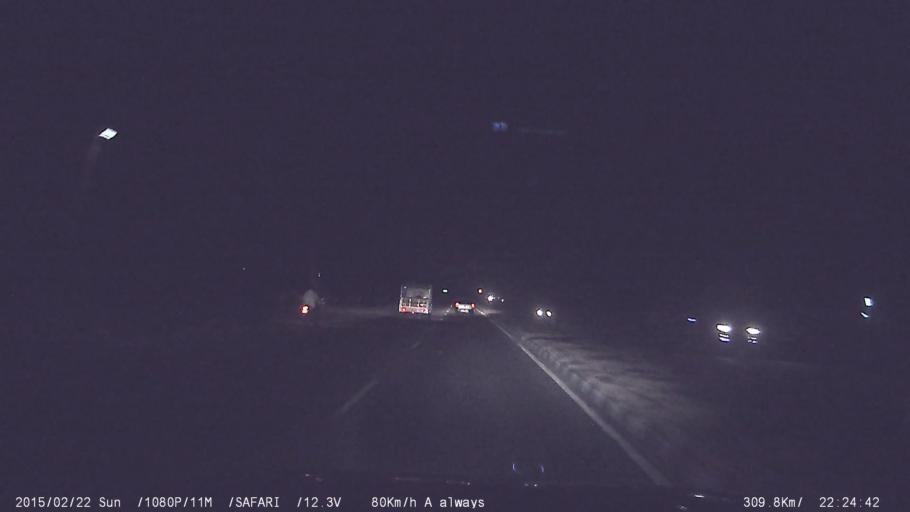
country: IN
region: Tamil Nadu
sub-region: Namakkal
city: Mohanur
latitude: 11.0400
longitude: 78.0592
